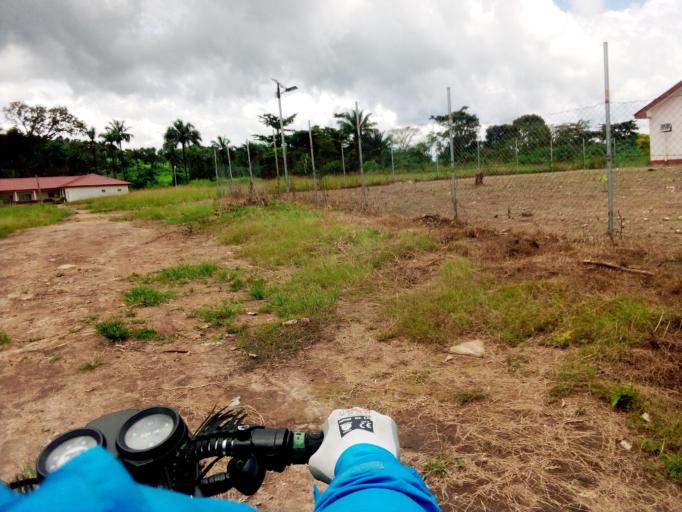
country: SL
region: Eastern Province
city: Giehun
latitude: 8.5571
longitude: -10.9850
